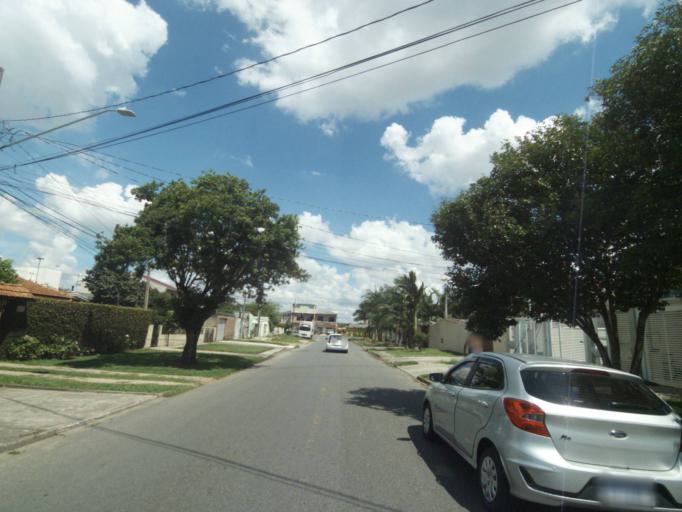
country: BR
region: Parana
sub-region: Pinhais
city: Pinhais
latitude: -25.4481
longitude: -49.2026
